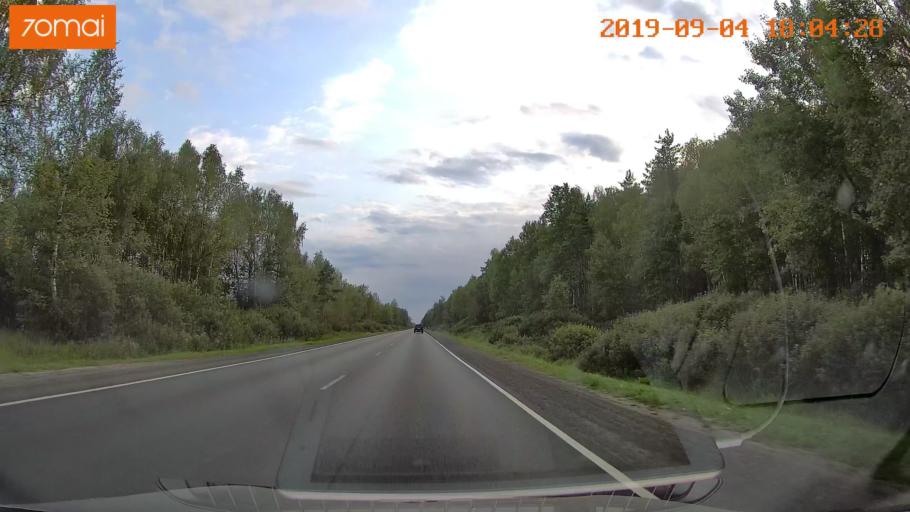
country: RU
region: Moskovskaya
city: Il'inskiy Pogost
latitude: 55.4519
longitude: 38.8388
